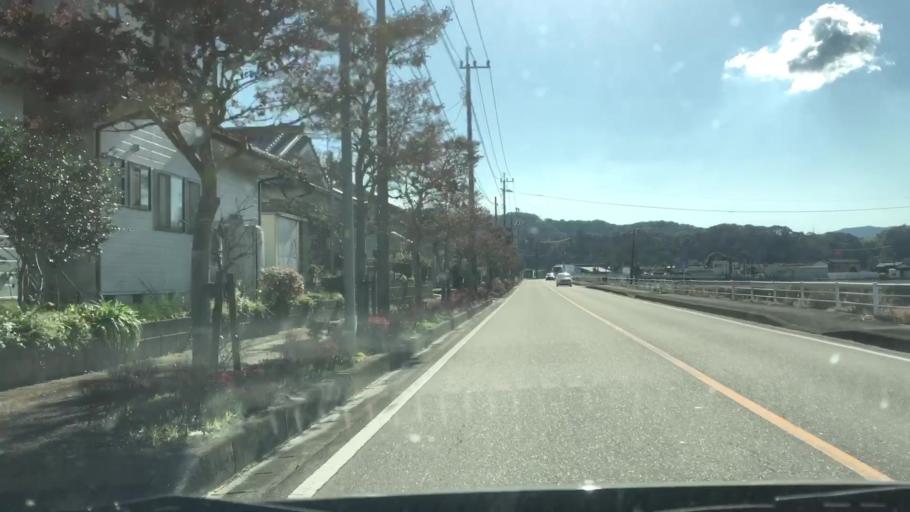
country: JP
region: Kagoshima
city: Satsumasendai
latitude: 31.8591
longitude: 130.3922
